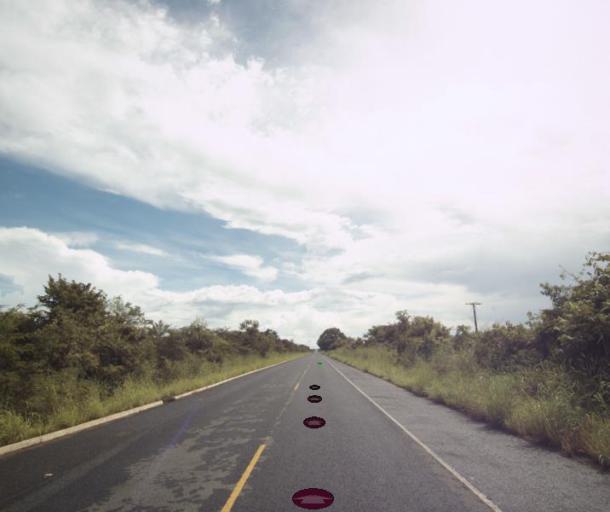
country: BR
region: Goias
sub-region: Sao Miguel Do Araguaia
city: Sao Miguel do Araguaia
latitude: -13.2952
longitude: -50.2337
